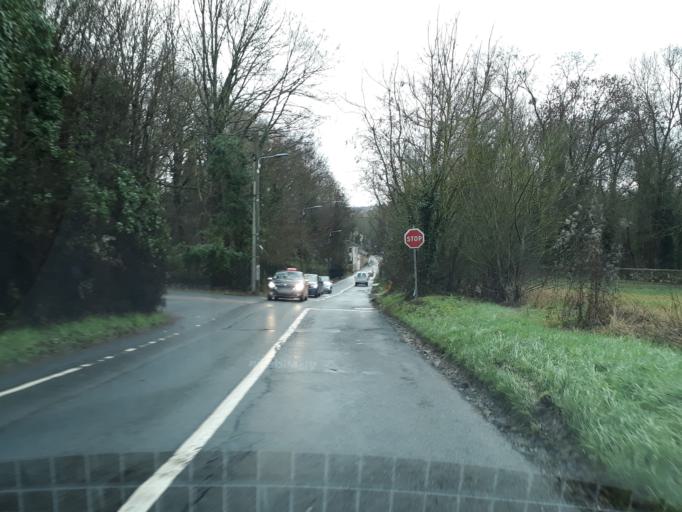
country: FR
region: Ile-de-France
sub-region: Departement de l'Essonne
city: Villabe
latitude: 48.5816
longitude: 2.4435
